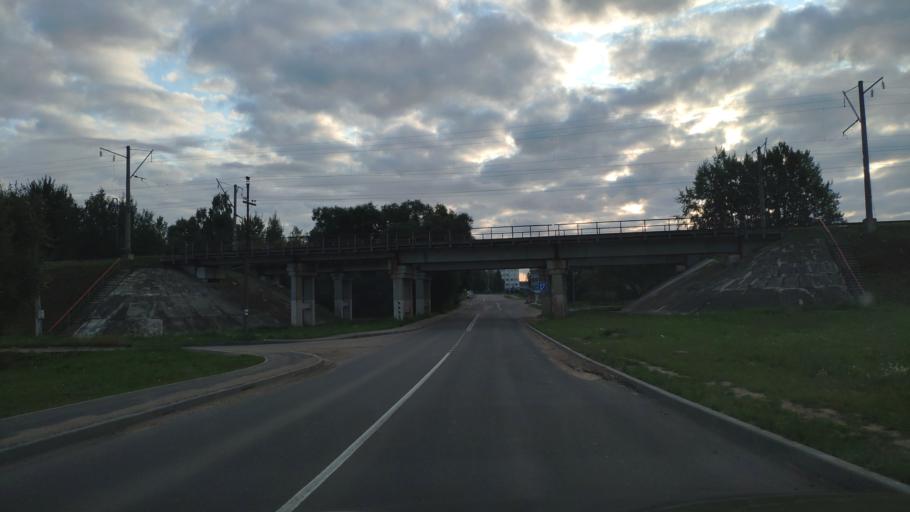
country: BY
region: Minsk
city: Azyartso
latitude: 53.8444
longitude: 27.4106
